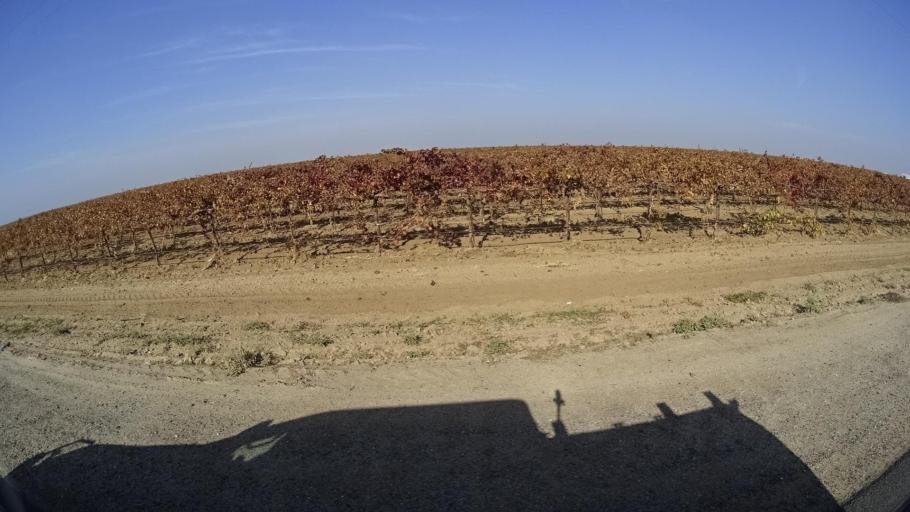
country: US
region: California
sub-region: Kern County
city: McFarland
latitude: 35.6021
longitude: -119.1573
